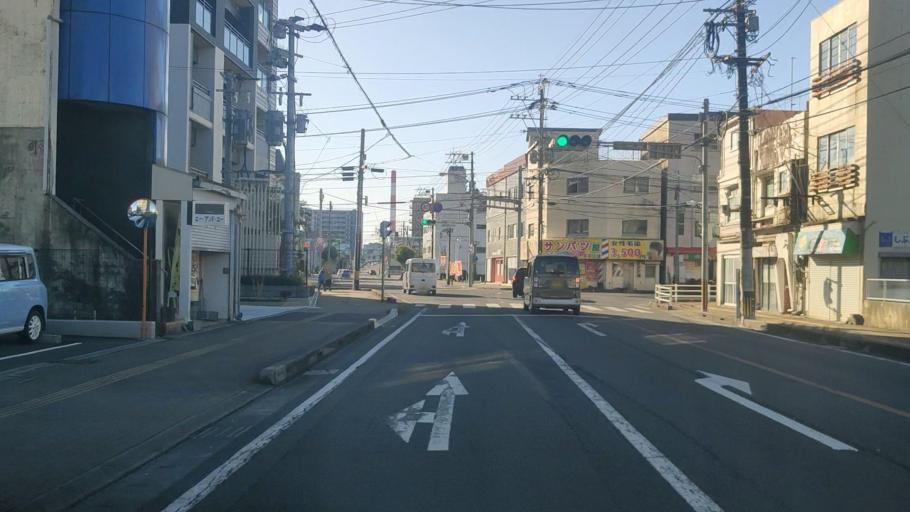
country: JP
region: Miyazaki
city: Nobeoka
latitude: 32.5874
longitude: 131.6711
